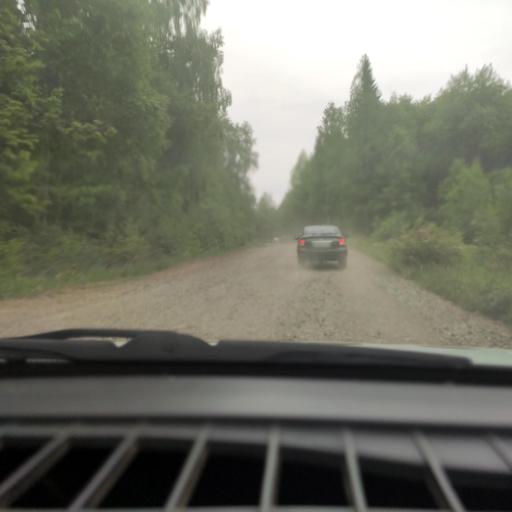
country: RU
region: Perm
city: Novyye Lyady
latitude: 57.9052
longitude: 56.6555
